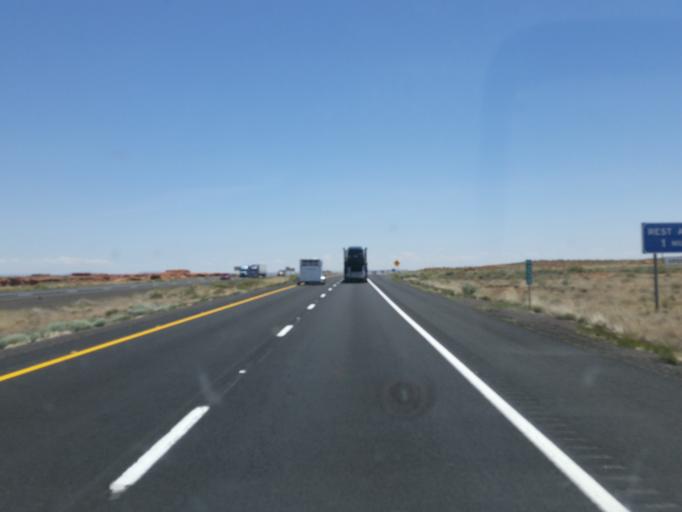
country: US
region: Arizona
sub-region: Coconino County
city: LeChee
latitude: 35.1100
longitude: -111.0296
